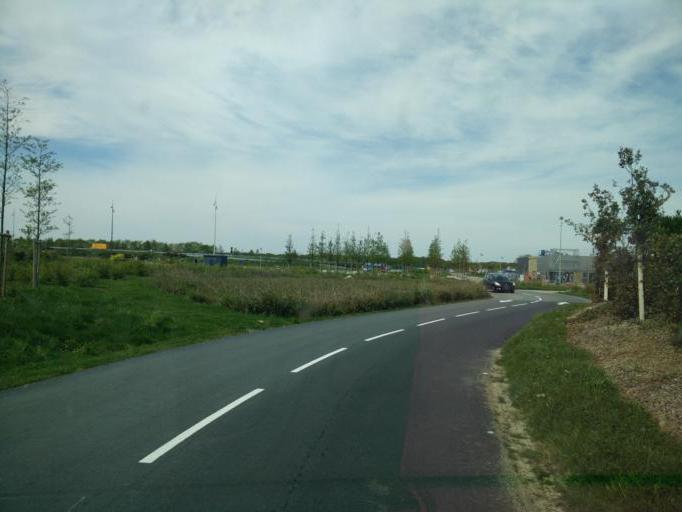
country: FR
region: Brittany
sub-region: Departement d'Ille-et-Vilaine
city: Dinard
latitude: 48.6084
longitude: -2.0634
